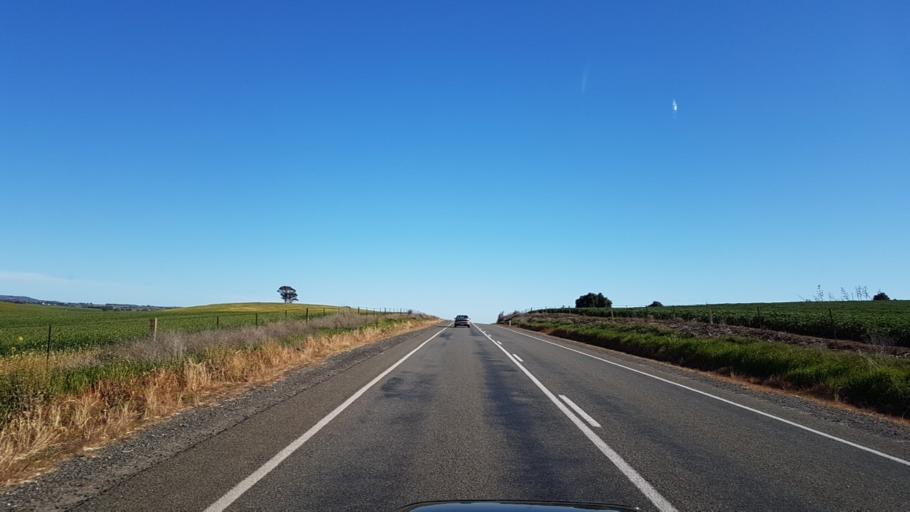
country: AU
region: South Australia
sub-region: Clare and Gilbert Valleys
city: Clare
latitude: -34.0641
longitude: 138.7922
